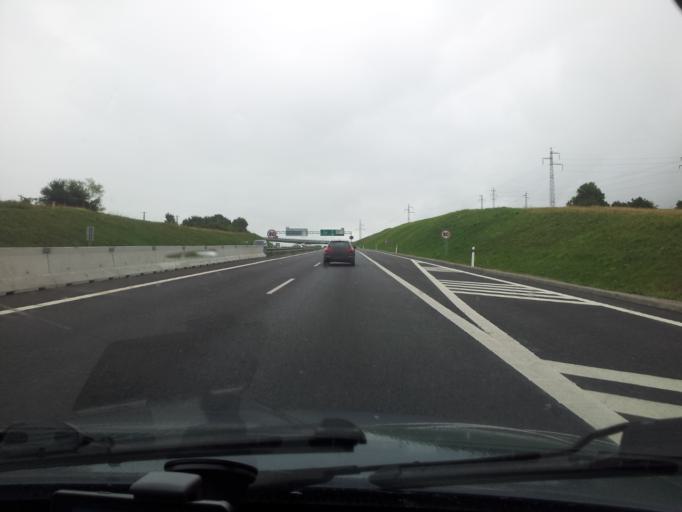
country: SK
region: Banskobystricky
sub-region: Okres Banska Bystrica
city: Banska Bystrica
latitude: 48.7492
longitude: 19.1458
